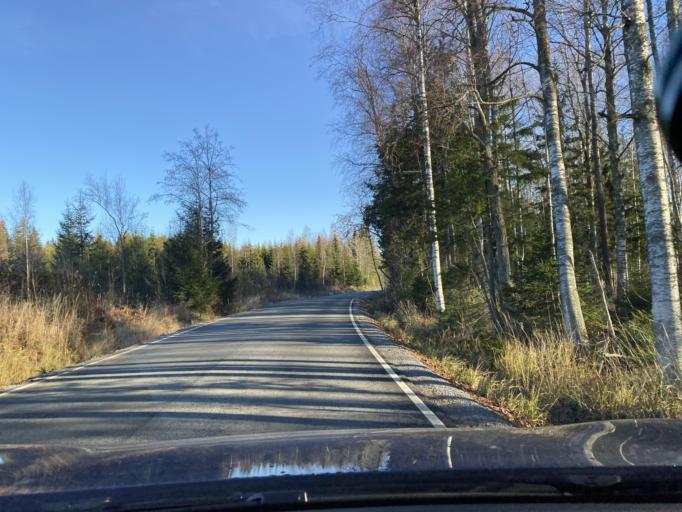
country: FI
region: Haeme
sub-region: Haemeenlinna
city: Kalvola
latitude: 61.0250
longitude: 24.1618
